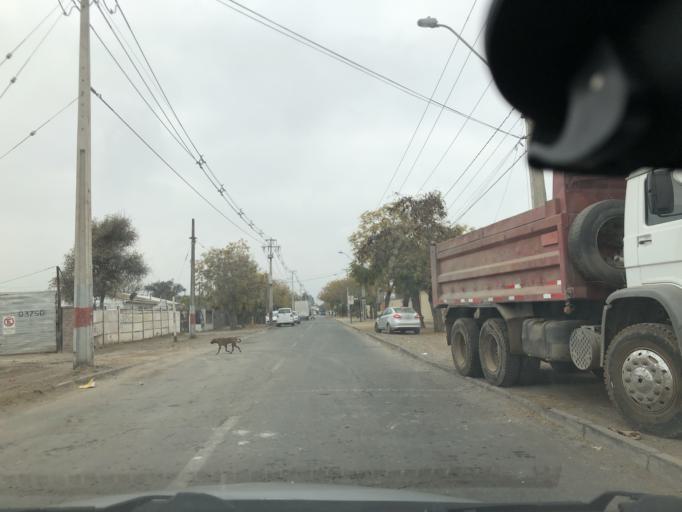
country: CL
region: Santiago Metropolitan
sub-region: Provincia de Santiago
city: La Pintana
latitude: -33.5808
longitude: -70.6100
